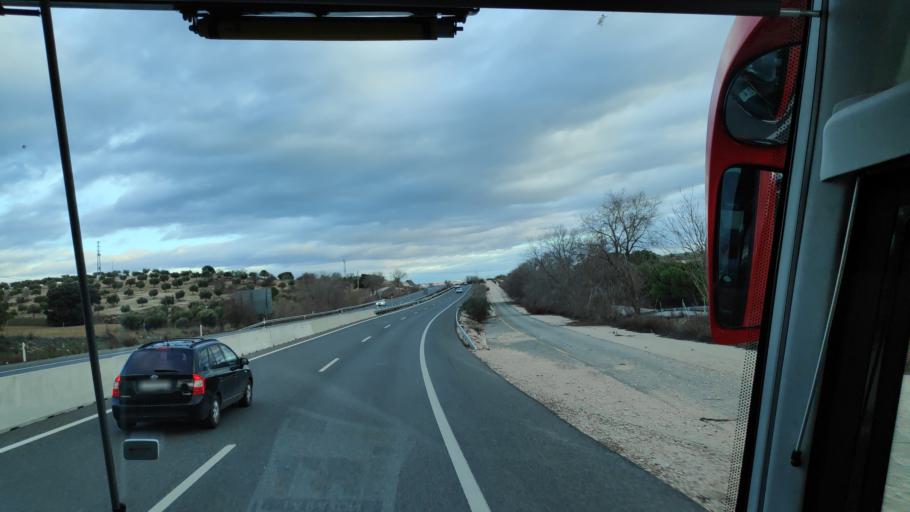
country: ES
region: Madrid
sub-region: Provincia de Madrid
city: Villarejo de Salvanes
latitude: 40.1558
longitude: -3.2536
